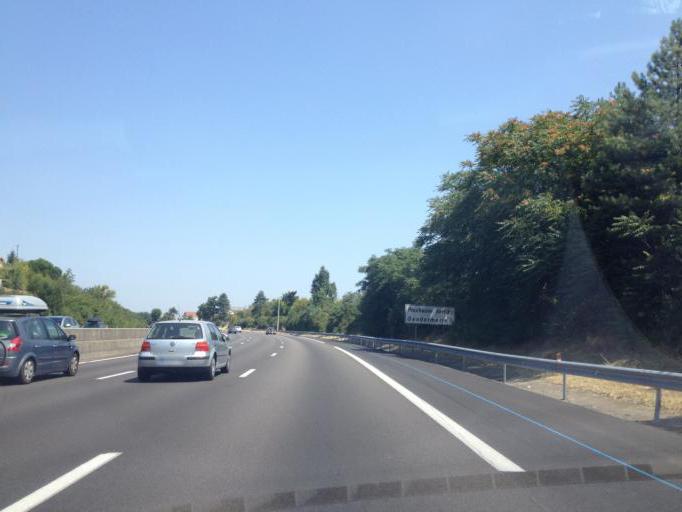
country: FR
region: Rhone-Alpes
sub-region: Departement de la Drome
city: Valence
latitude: 44.9451
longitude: 4.8908
